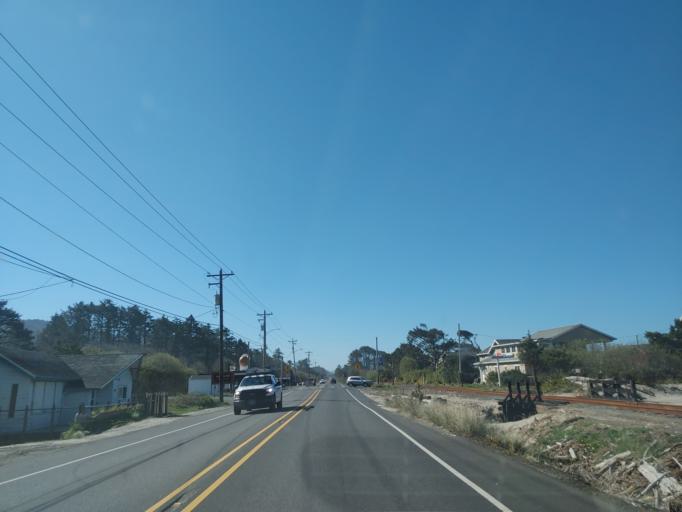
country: US
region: Oregon
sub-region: Tillamook County
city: Rockaway Beach
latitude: 45.6056
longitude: -123.9452
